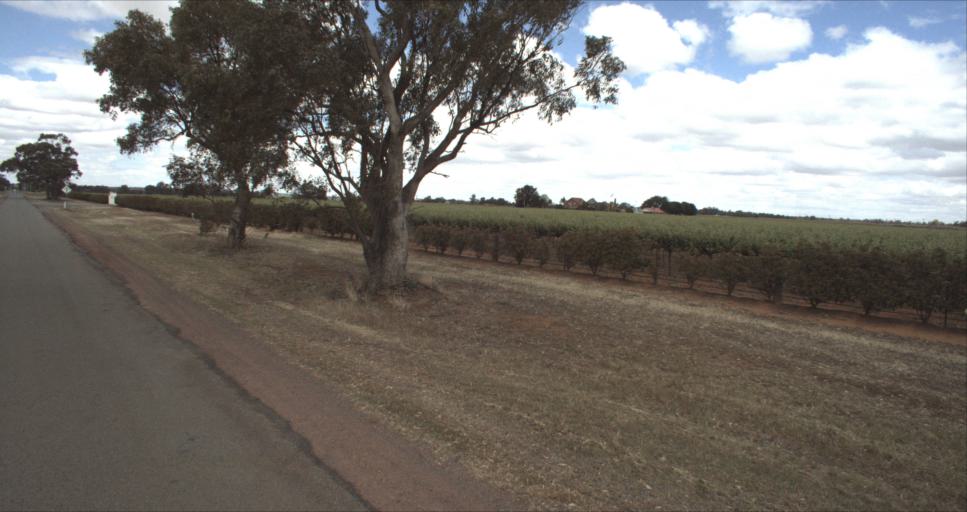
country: AU
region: New South Wales
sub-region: Leeton
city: Leeton
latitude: -34.5886
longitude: 146.3869
